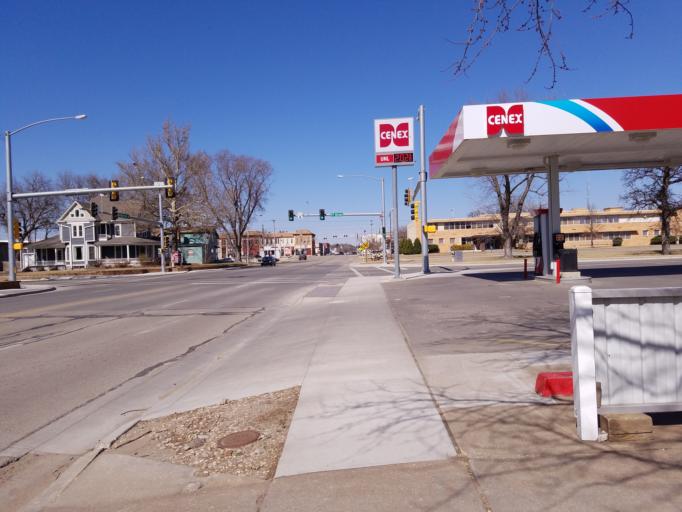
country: US
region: Kansas
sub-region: Dickinson County
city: Abilene
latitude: 38.9148
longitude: -97.2138
